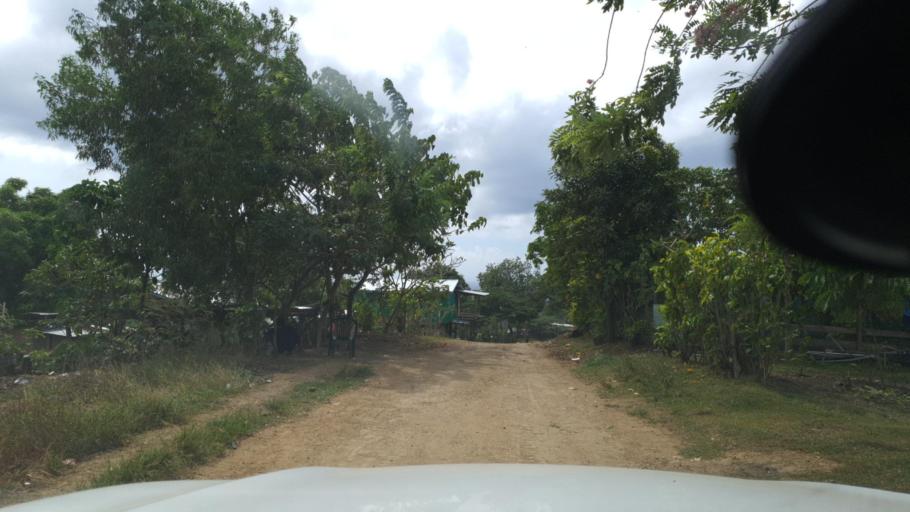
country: SB
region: Guadalcanal
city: Honiara
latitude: -9.4324
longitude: 159.9289
